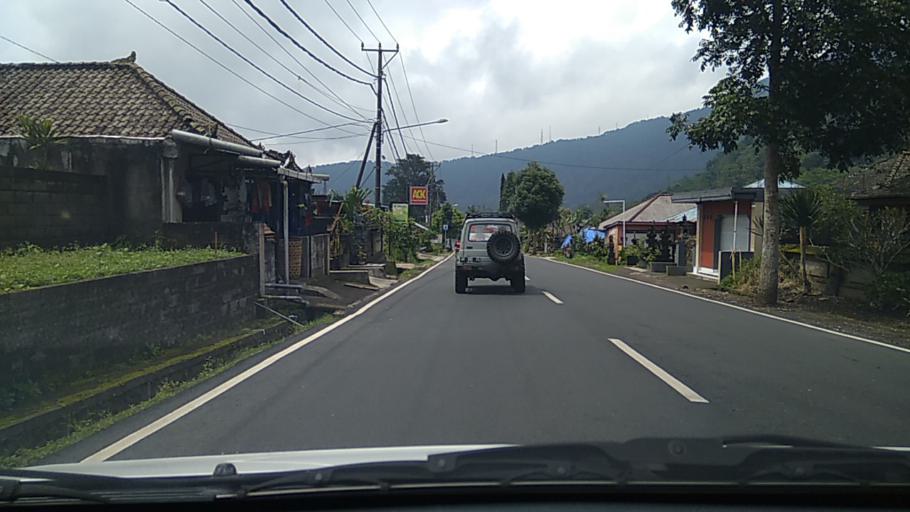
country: ID
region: Bali
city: Munduk
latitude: -8.2593
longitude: 115.1627
